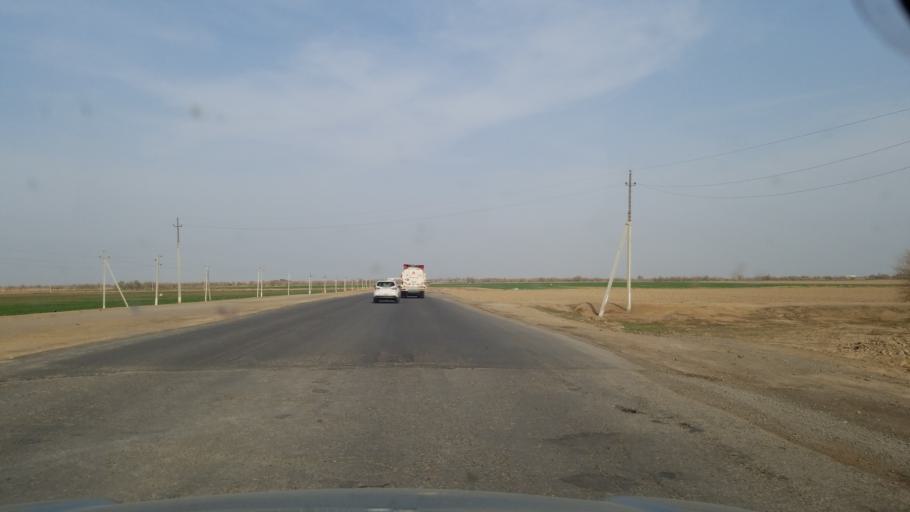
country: TM
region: Mary
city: Bayramaly
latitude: 37.6130
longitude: 62.2882
